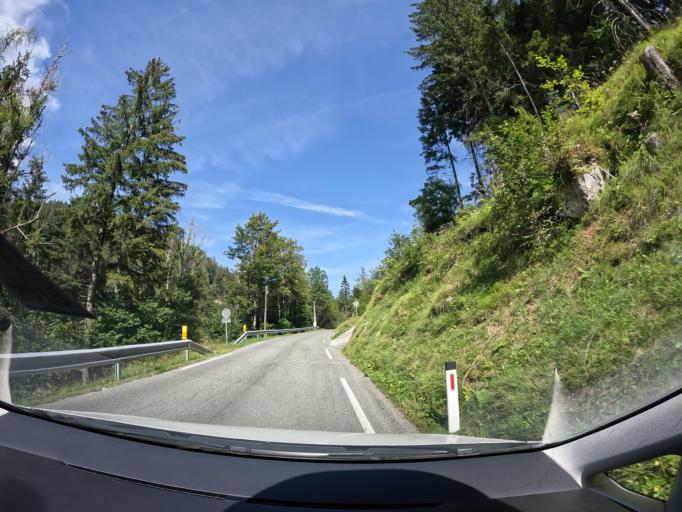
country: AT
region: Carinthia
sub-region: Politischer Bezirk Villach Land
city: Sankt Jakob
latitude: 46.5607
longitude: 14.0765
